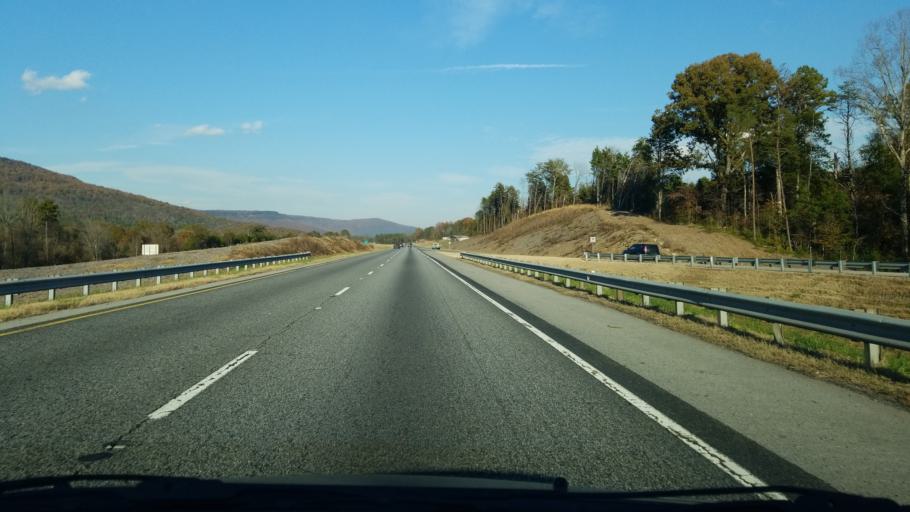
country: US
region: Georgia
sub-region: Dade County
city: Trenton
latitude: 34.9437
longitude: -85.4739
